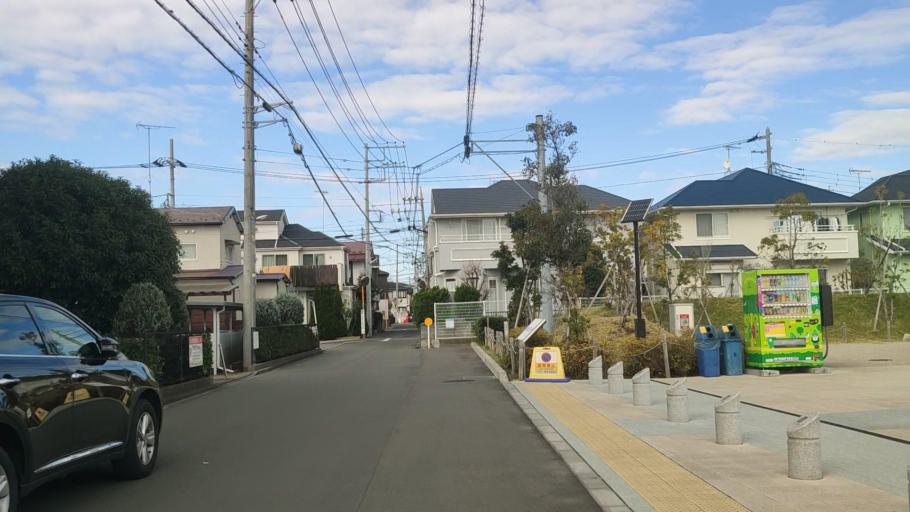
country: JP
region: Kanagawa
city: Minami-rinkan
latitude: 35.4888
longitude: 139.4382
